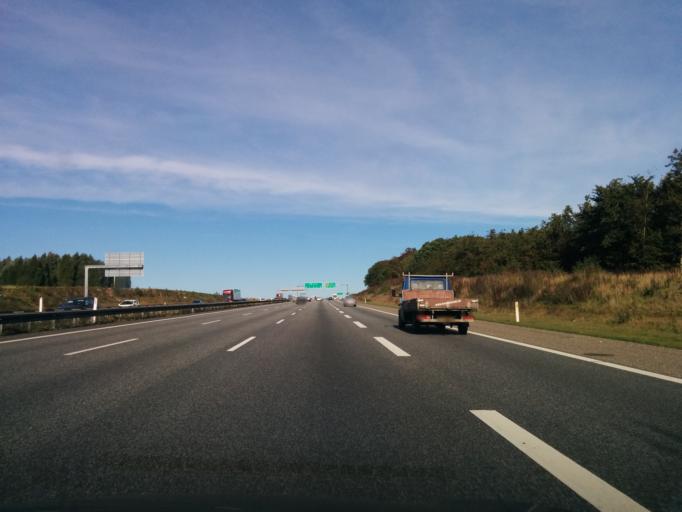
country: DK
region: South Denmark
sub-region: Vejle Kommune
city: Vejle
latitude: 55.7294
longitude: 9.5765
